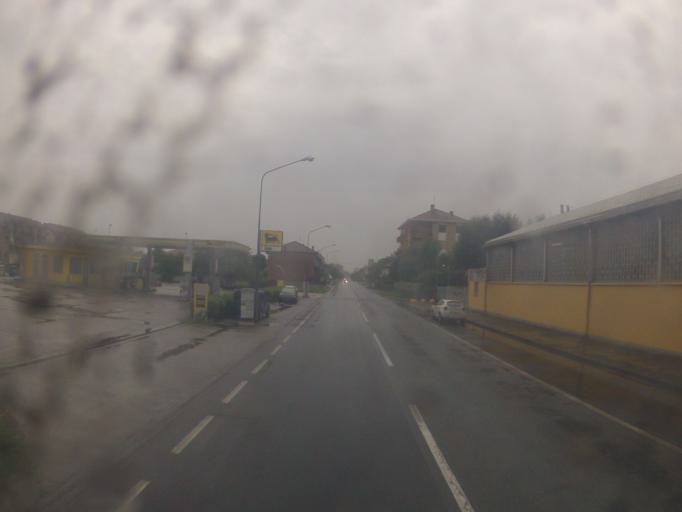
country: IT
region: Piedmont
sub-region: Provincia di Torino
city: La Loggia
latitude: 44.9484
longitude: 7.6693
